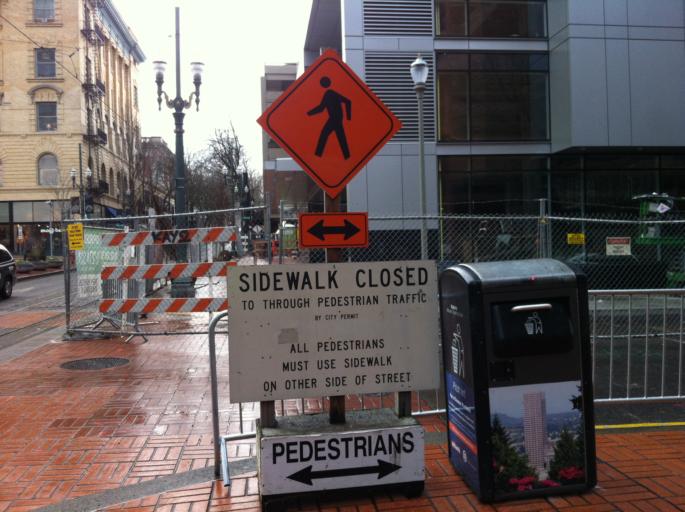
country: US
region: Oregon
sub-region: Multnomah County
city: Portland
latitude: 45.5188
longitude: -122.6809
